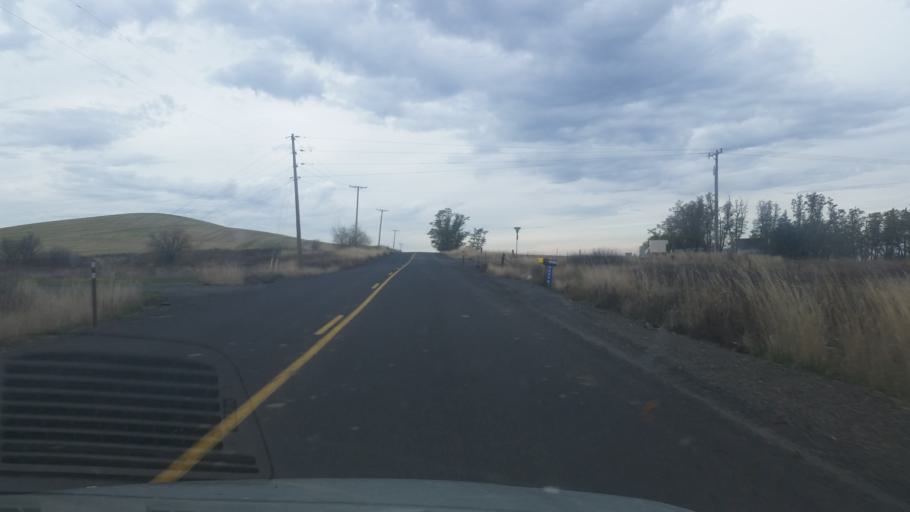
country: US
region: Washington
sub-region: Spokane County
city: Cheney
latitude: 47.3907
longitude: -117.4657
